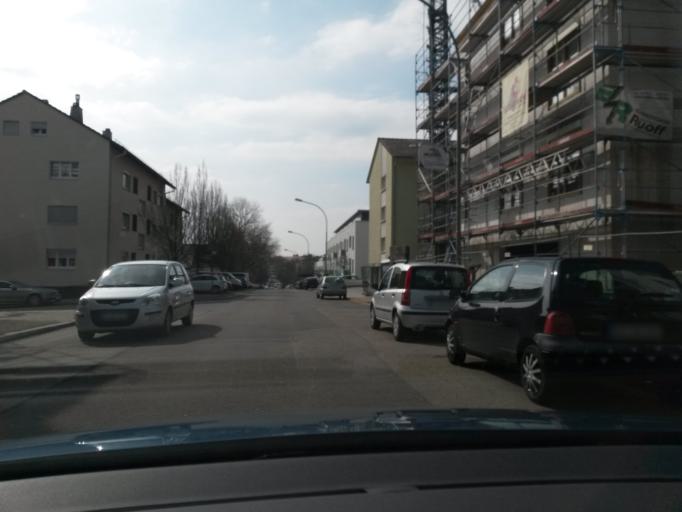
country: DE
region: Baden-Wuerttemberg
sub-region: Karlsruhe Region
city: Pforzheim
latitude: 48.9004
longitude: 8.7169
